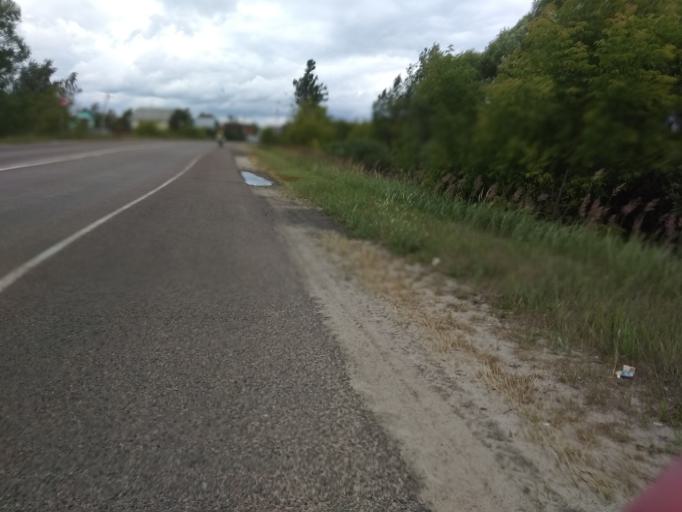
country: RU
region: Moskovskaya
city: Kerva
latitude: 55.5914
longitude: 39.7008
